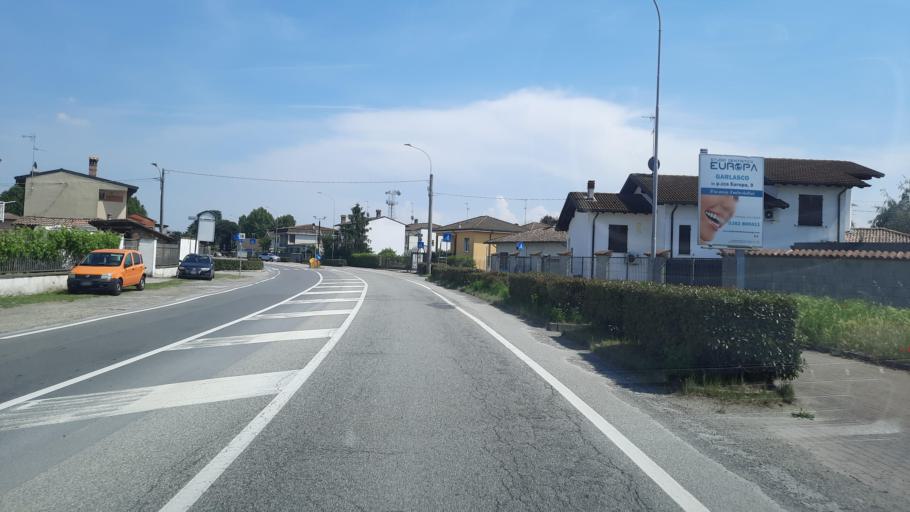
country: IT
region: Lombardy
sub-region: Provincia di Pavia
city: Garlasco
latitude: 45.1932
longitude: 8.9143
